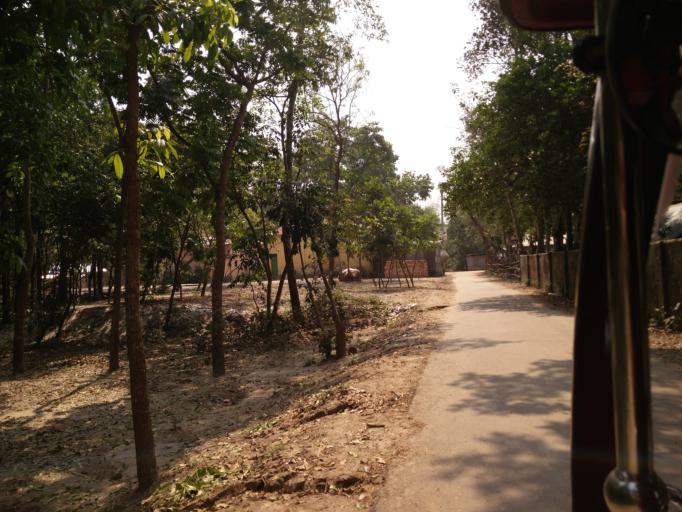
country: BD
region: Dhaka
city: Muktagacha
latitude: 24.8989
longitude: 90.2594
